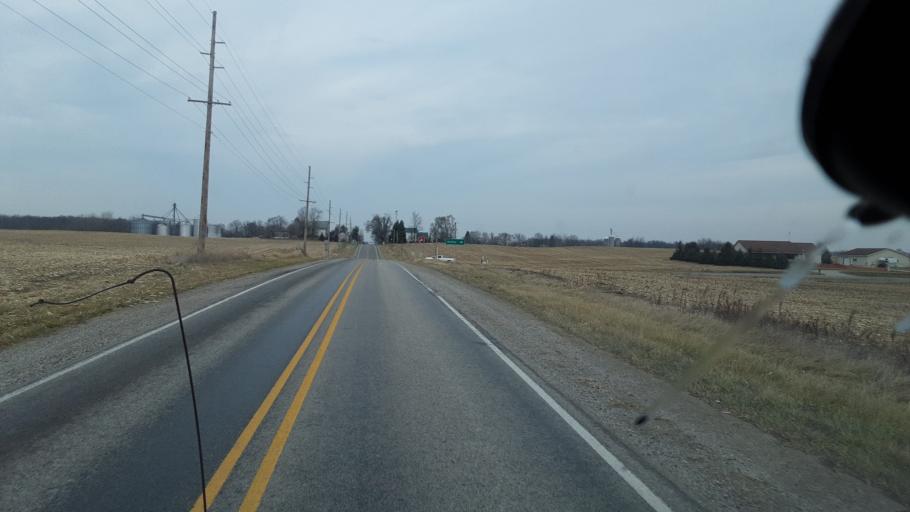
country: US
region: Indiana
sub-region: Noble County
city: Kendallville
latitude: 41.5252
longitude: -85.1706
